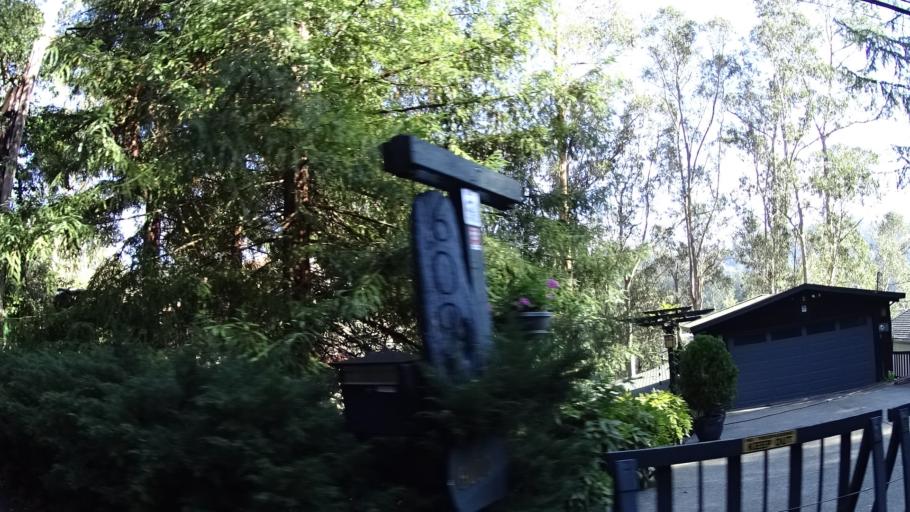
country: US
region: California
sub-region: Alameda County
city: Piedmont
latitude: 37.8400
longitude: -122.2117
